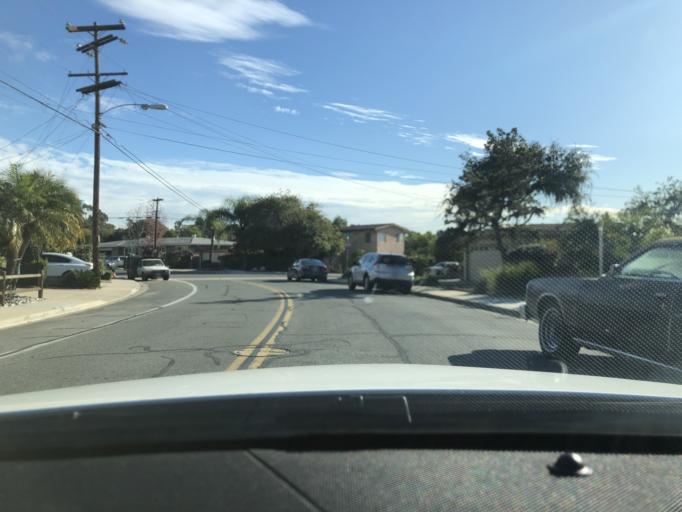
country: US
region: California
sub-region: San Diego County
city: Lemon Grove
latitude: 32.7522
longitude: -117.0714
